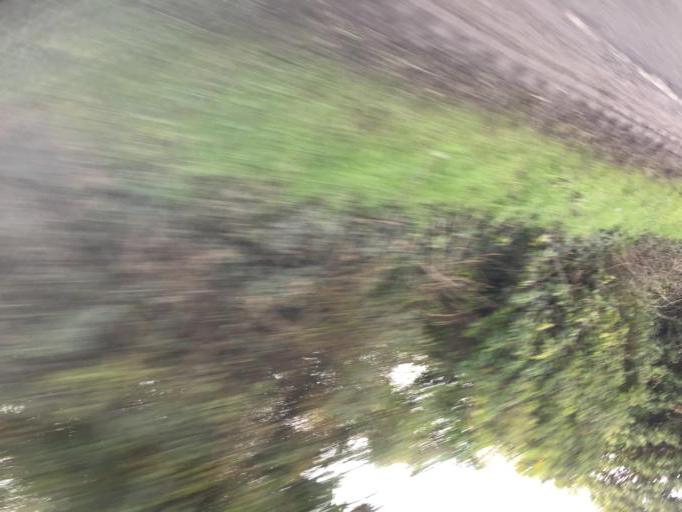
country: GB
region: England
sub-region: Oxfordshire
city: Blewbury
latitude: 51.5656
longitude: -1.2146
